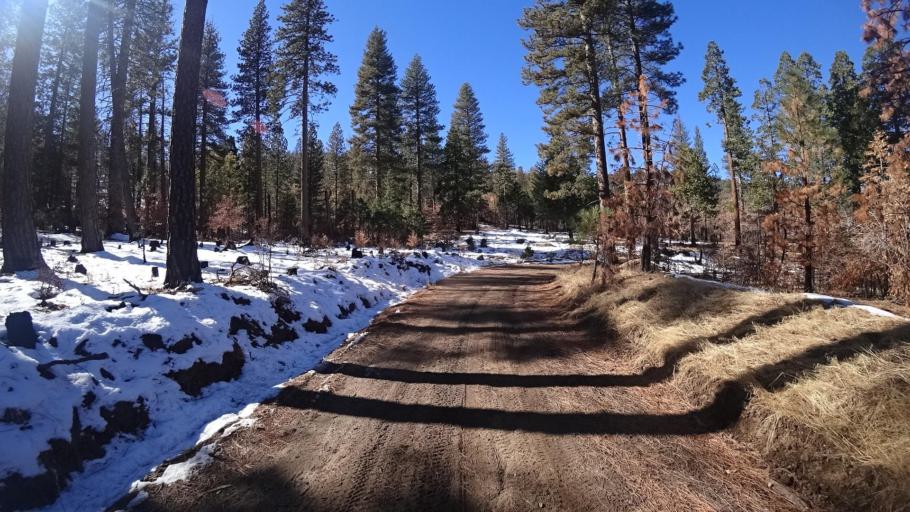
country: US
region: California
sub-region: Kern County
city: Alta Sierra
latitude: 35.7155
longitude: -118.5348
